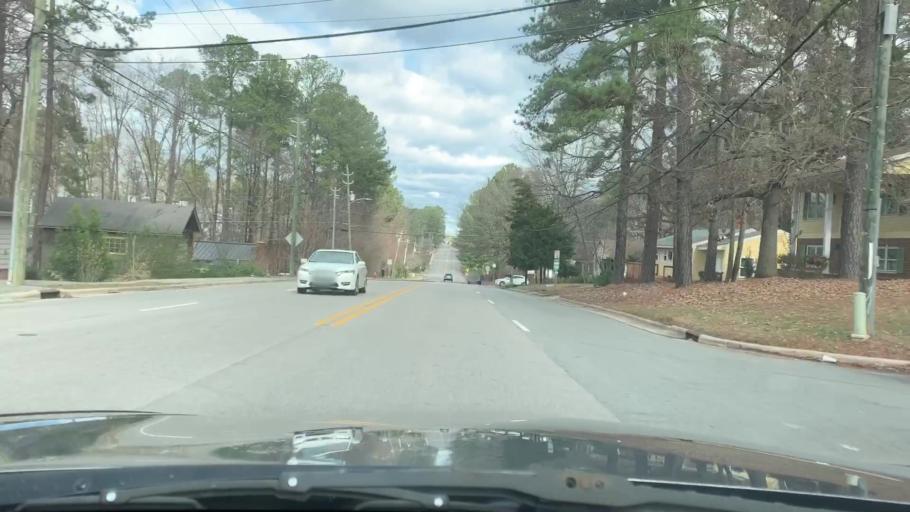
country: US
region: North Carolina
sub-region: Wake County
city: Cary
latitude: 35.7936
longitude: -78.7831
